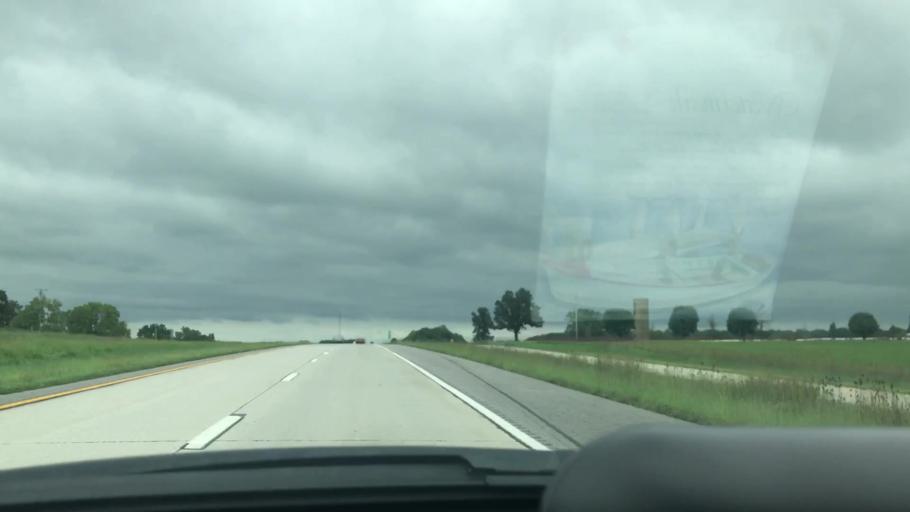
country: US
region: Missouri
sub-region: Greene County
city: Fair Grove
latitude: 37.4357
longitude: -93.1445
